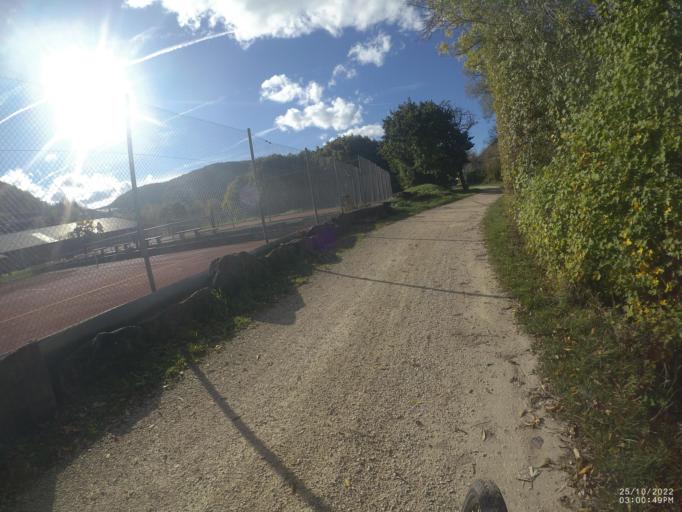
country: DE
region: Baden-Wuerttemberg
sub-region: Regierungsbezirk Stuttgart
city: Bad Ditzenbach
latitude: 48.5805
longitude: 9.6856
